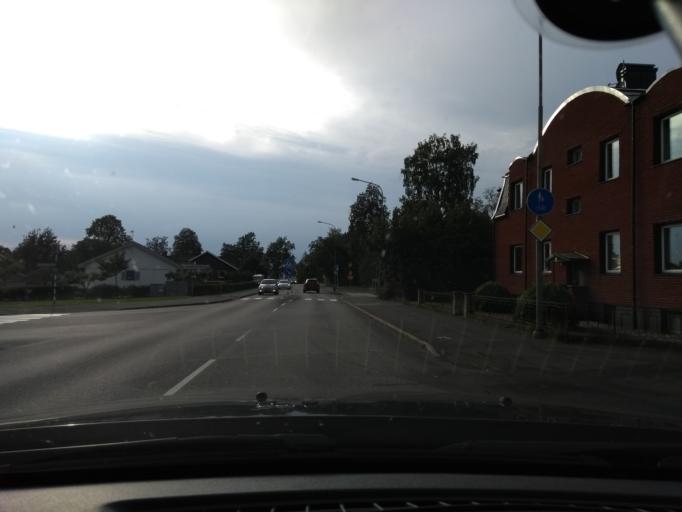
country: SE
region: Joenkoeping
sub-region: Nassjo Kommun
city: Nassjo
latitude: 57.6498
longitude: 14.7131
